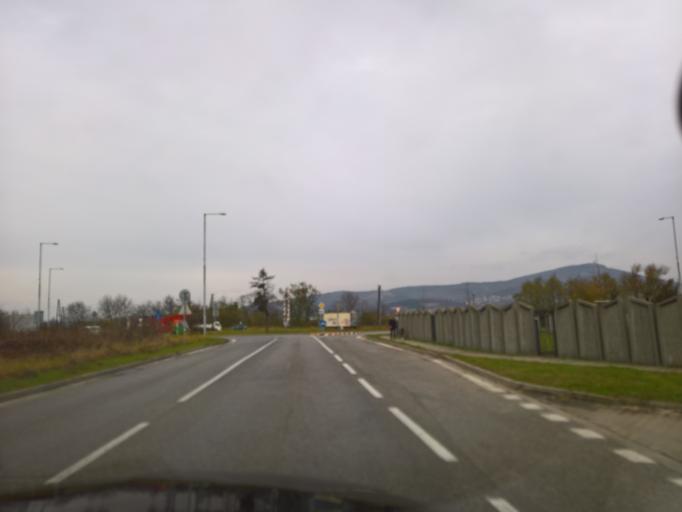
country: SK
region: Nitriansky
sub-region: Okres Nitra
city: Nitra
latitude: 48.3146
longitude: 18.0516
